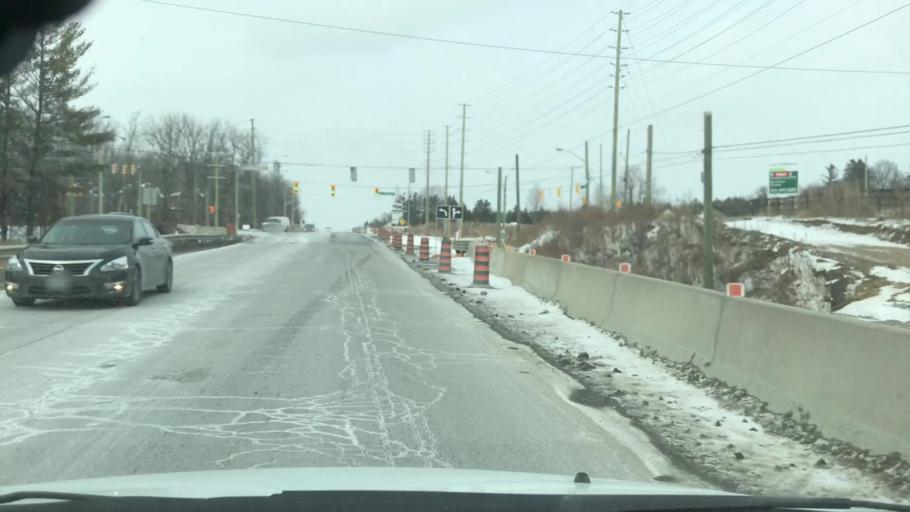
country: CA
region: Ontario
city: Newmarket
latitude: 44.0281
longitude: -79.4226
